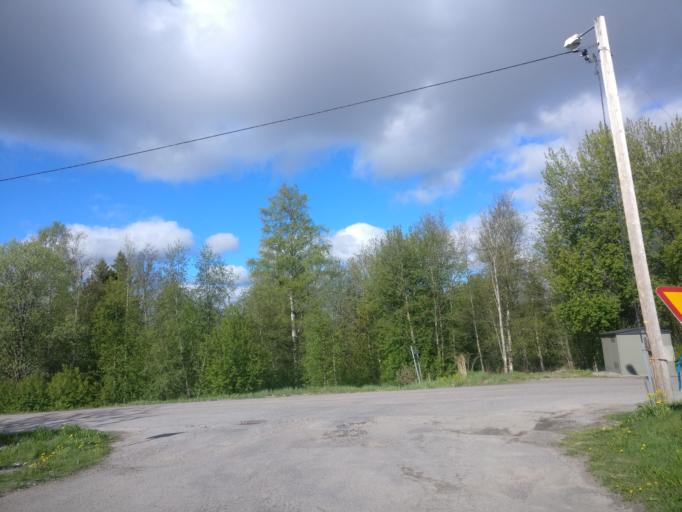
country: SE
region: Vaesternorrland
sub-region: Sundsvalls Kommun
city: Johannedal
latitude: 62.4122
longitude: 17.4151
